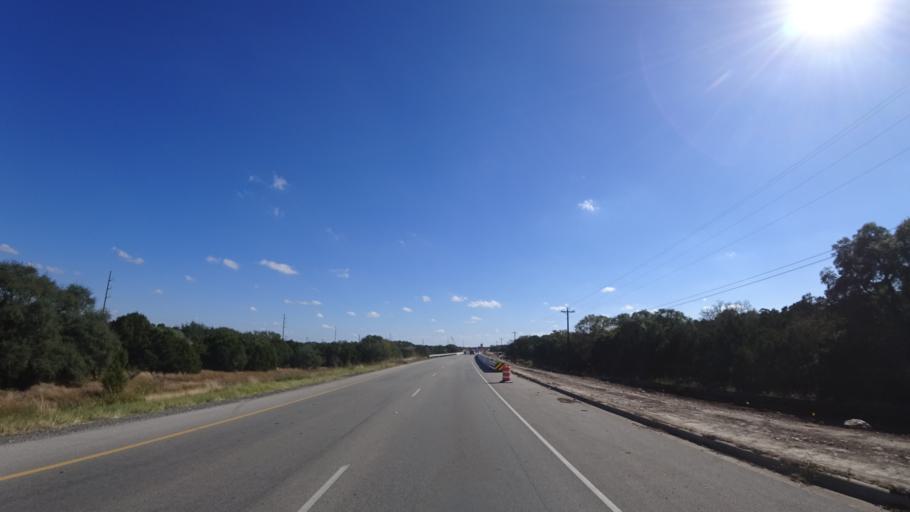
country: US
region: Texas
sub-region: Travis County
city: Shady Hollow
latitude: 30.1784
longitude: -97.8955
